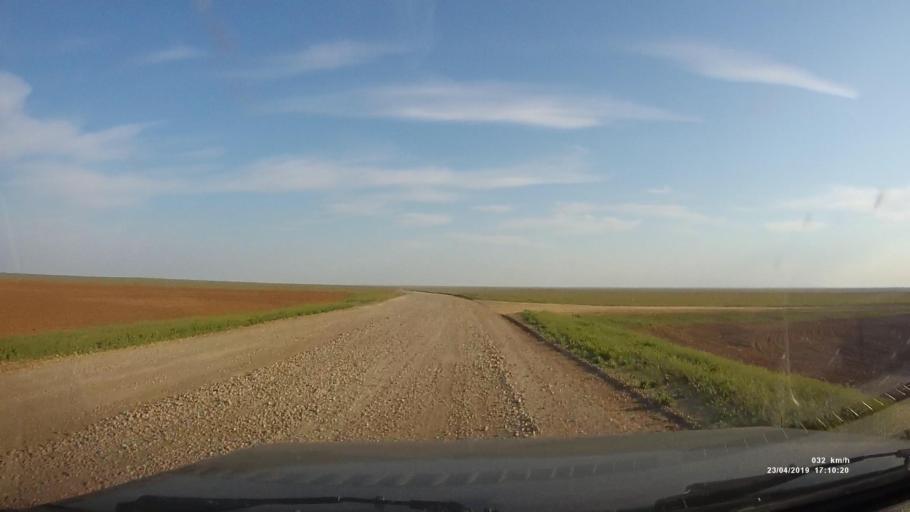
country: RU
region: Kalmykiya
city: Priyutnoye
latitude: 46.2472
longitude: 43.4841
